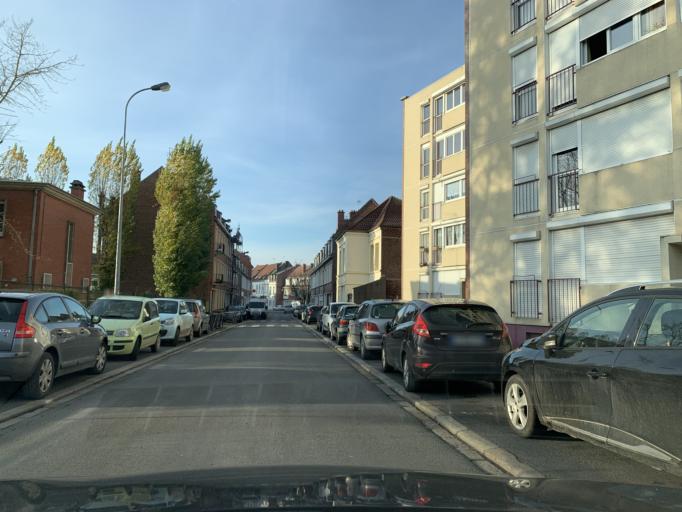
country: FR
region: Nord-Pas-de-Calais
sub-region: Departement du Nord
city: Neuville-Saint-Remy
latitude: 50.1759
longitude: 3.2271
